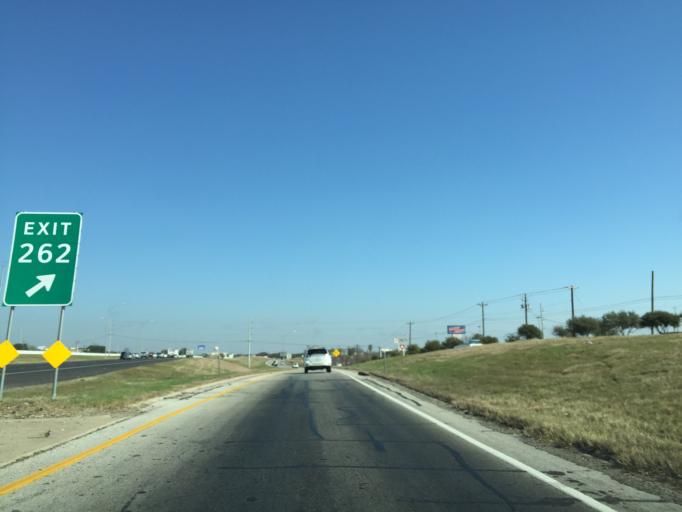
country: US
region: Texas
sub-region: Williamson County
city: Georgetown
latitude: 30.6349
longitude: -97.6905
